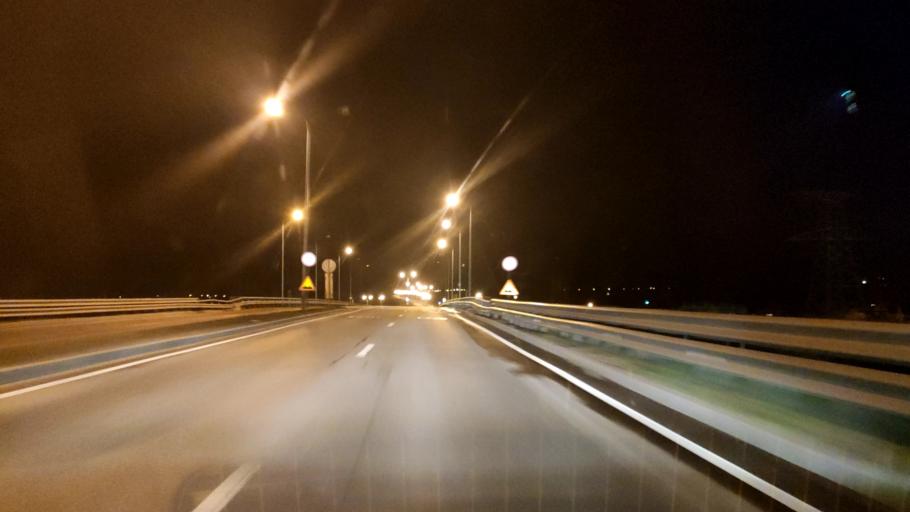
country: RU
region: Belgorod
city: Staryy Oskol
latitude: 51.2985
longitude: 37.7718
